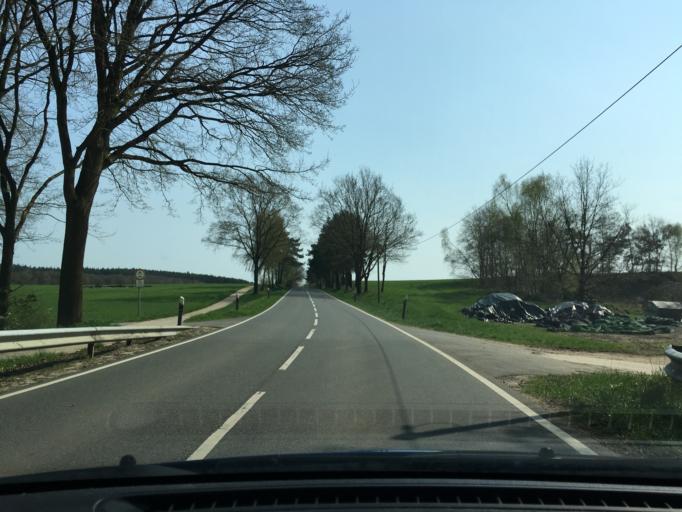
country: DE
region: Lower Saxony
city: Sudergellersen
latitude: 53.2036
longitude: 10.3008
